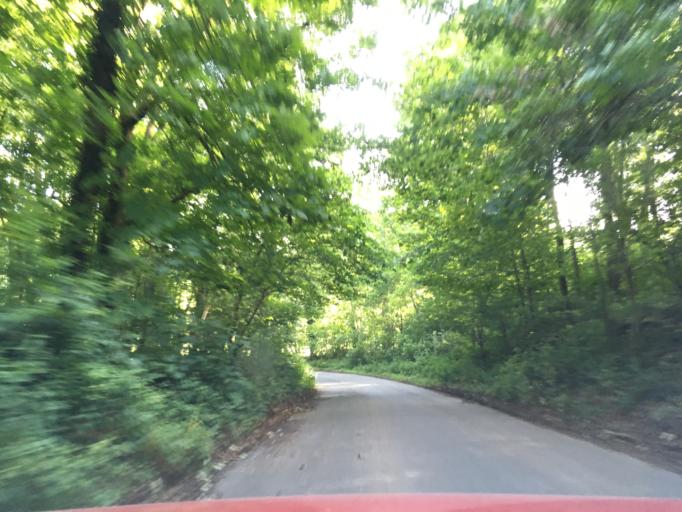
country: GB
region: England
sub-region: Gloucestershire
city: Lechlade
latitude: 51.7618
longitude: -1.7234
